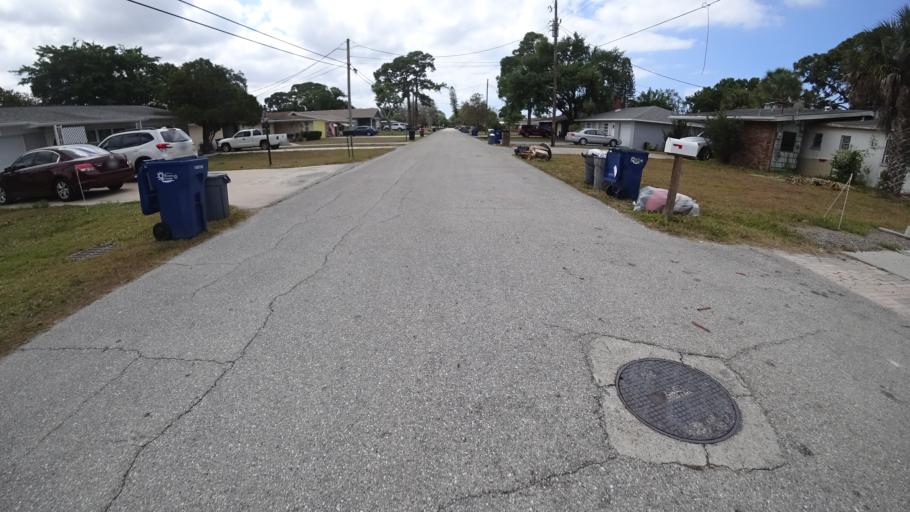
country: US
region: Florida
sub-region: Manatee County
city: Bayshore Gardens
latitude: 27.4431
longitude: -82.5830
